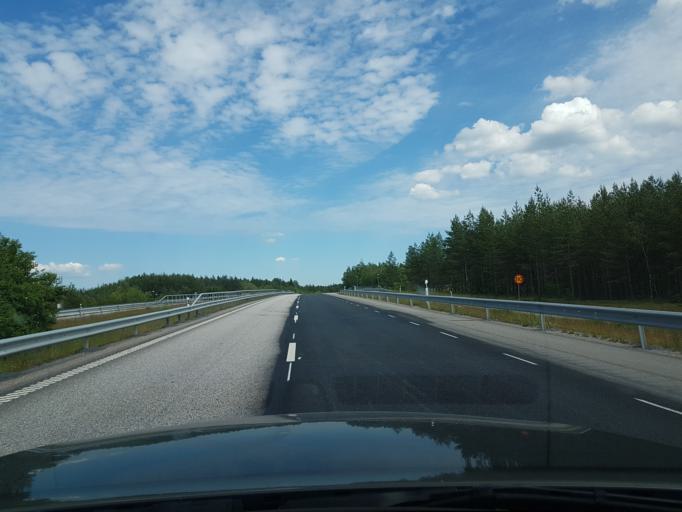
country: SE
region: Stockholm
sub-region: Norrtalje Kommun
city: Rimbo
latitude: 59.7023
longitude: 18.4880
